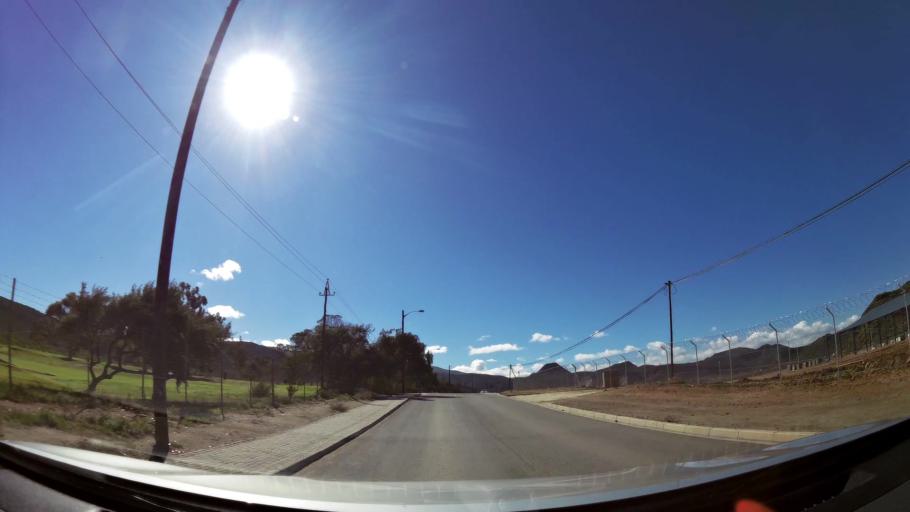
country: ZA
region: Western Cape
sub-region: Cape Winelands District Municipality
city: Ashton
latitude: -33.7733
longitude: 20.1356
